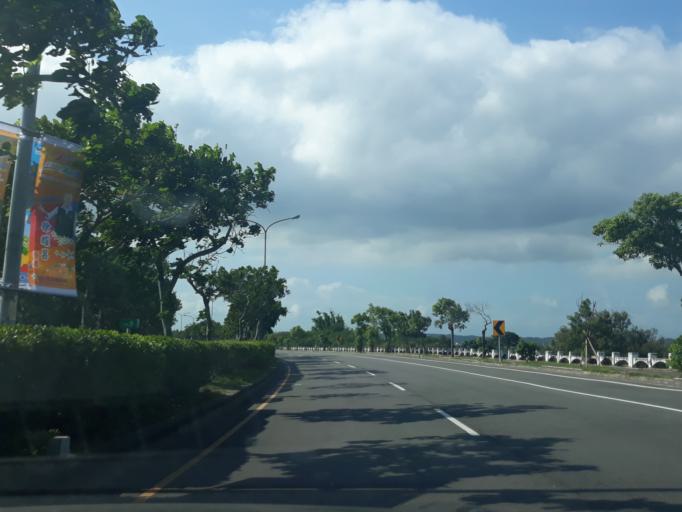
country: TW
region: Taiwan
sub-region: Miaoli
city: Miaoli
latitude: 24.5849
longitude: 120.8419
